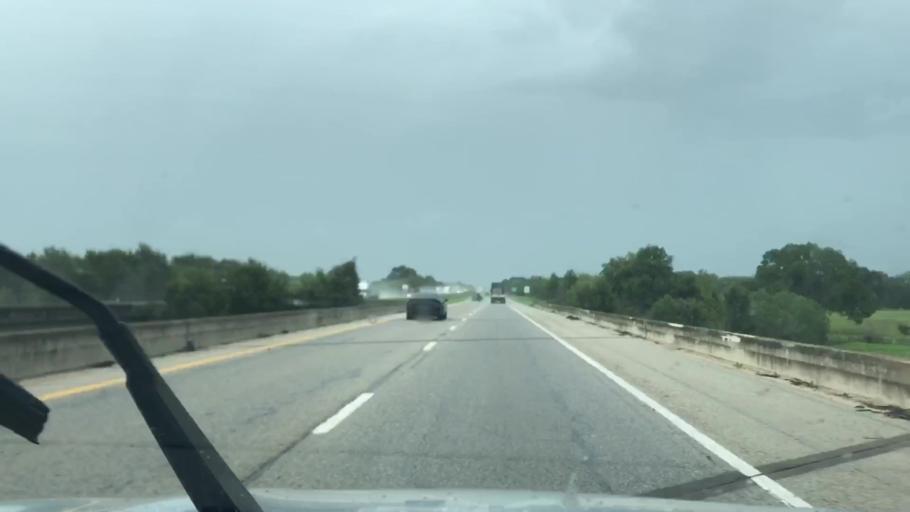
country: US
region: Texas
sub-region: Caldwell County
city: Luling
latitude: 29.6496
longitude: -97.6406
